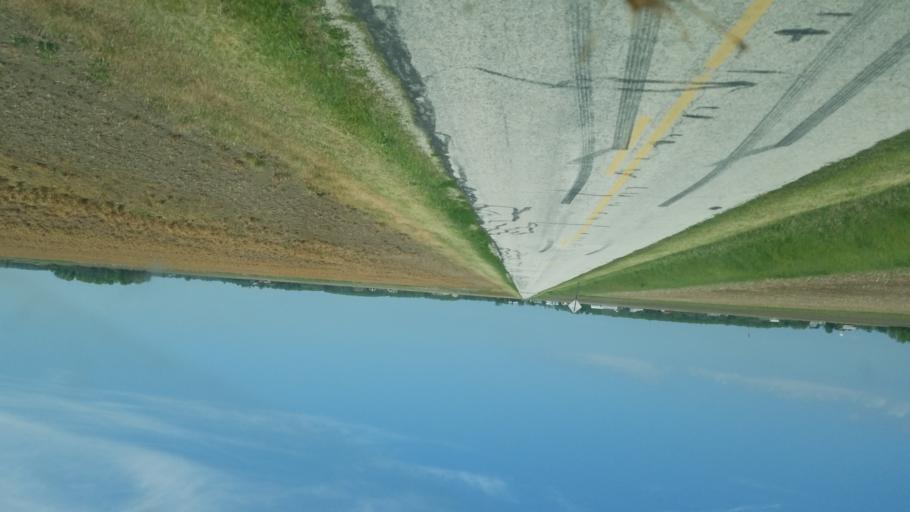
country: US
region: Ohio
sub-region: Ottawa County
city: Oak Harbor
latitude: 41.4592
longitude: -83.2017
